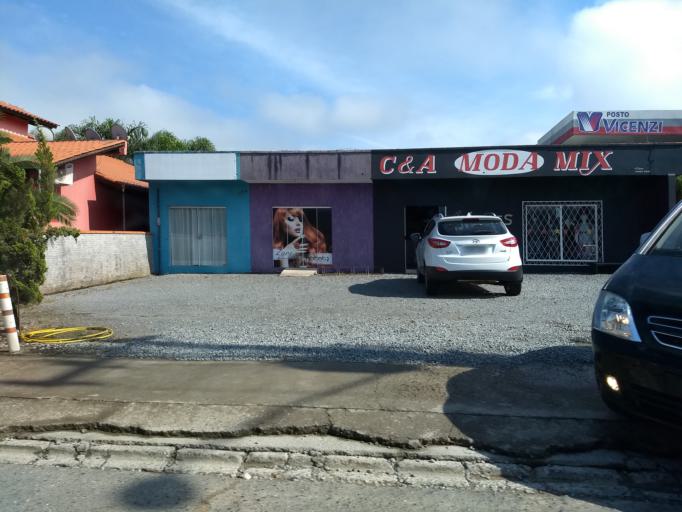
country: BR
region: Santa Catarina
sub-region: Schroeder
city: Schroeder
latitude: -26.4381
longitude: -49.1512
